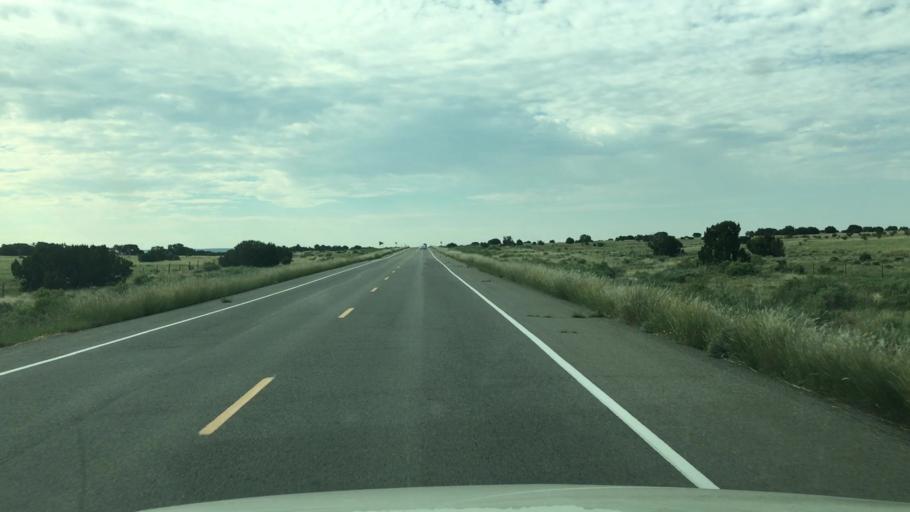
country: US
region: New Mexico
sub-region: Santa Fe County
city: Eldorado at Santa Fe
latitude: 35.4319
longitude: -105.8799
